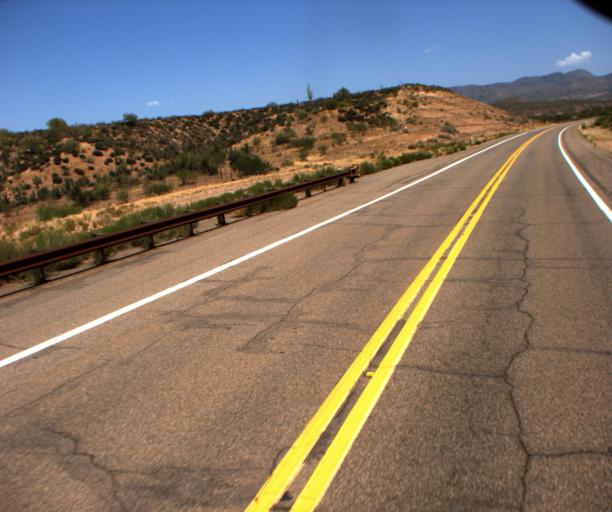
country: US
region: Arizona
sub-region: Gila County
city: Miami
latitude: 33.6115
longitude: -111.0159
